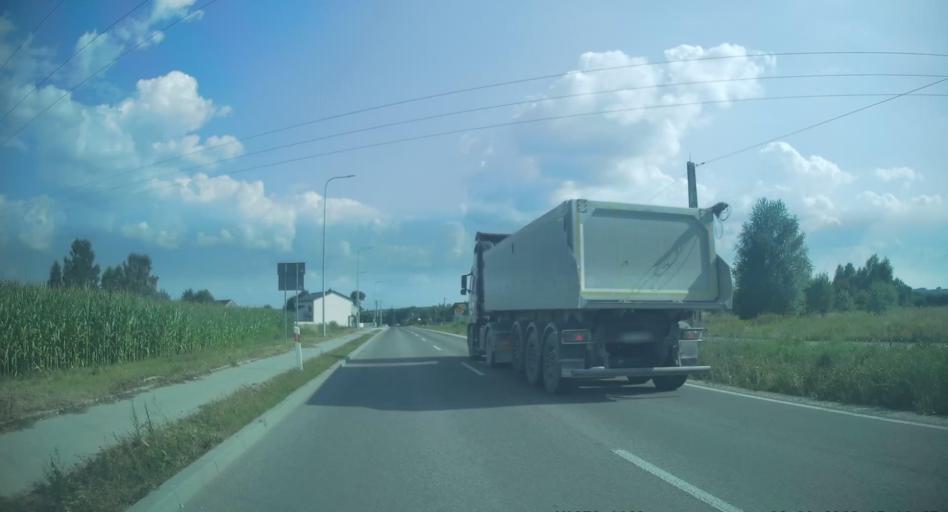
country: PL
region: Swietokrzyskie
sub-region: Powiat konecki
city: Radoszyce
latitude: 51.0668
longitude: 20.2714
